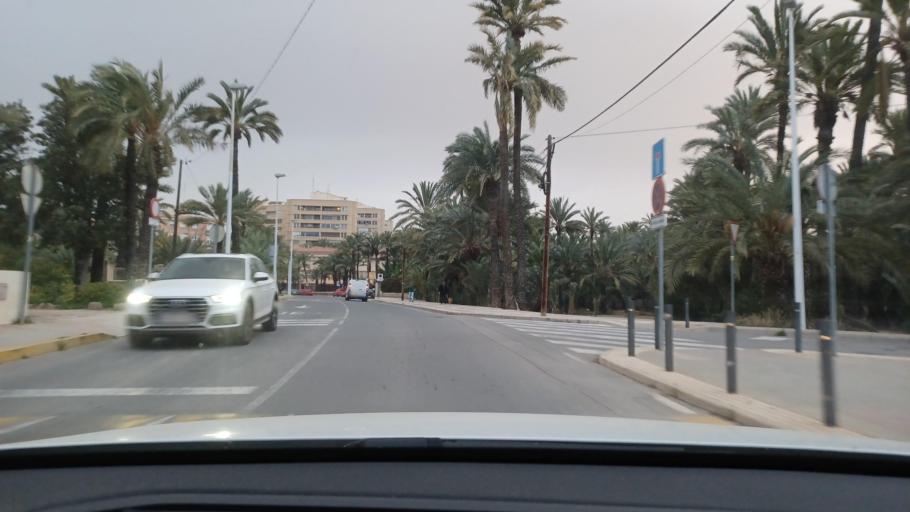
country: ES
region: Valencia
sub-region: Provincia de Alicante
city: Elche
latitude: 38.2603
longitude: -0.6931
